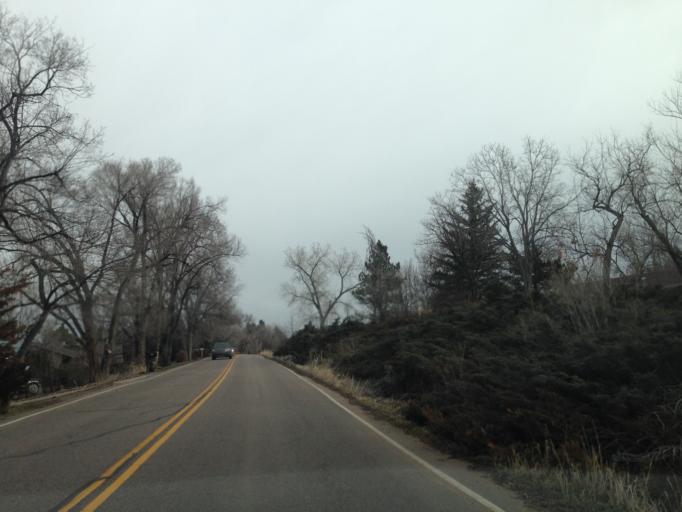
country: US
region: Colorado
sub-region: Boulder County
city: Gunbarrel
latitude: 40.0103
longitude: -105.1966
